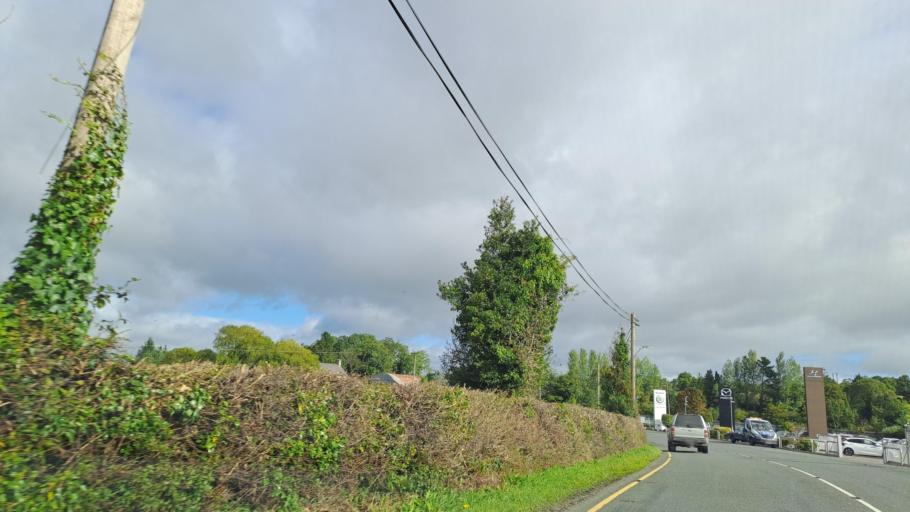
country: IE
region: Ulster
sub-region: County Monaghan
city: Carrickmacross
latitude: 53.9496
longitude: -6.7604
